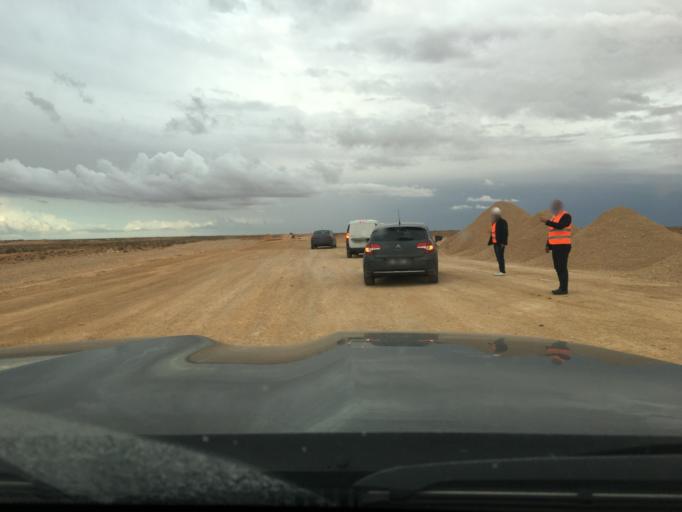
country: TN
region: Madanin
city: Medenine
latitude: 33.2603
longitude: 10.5757
